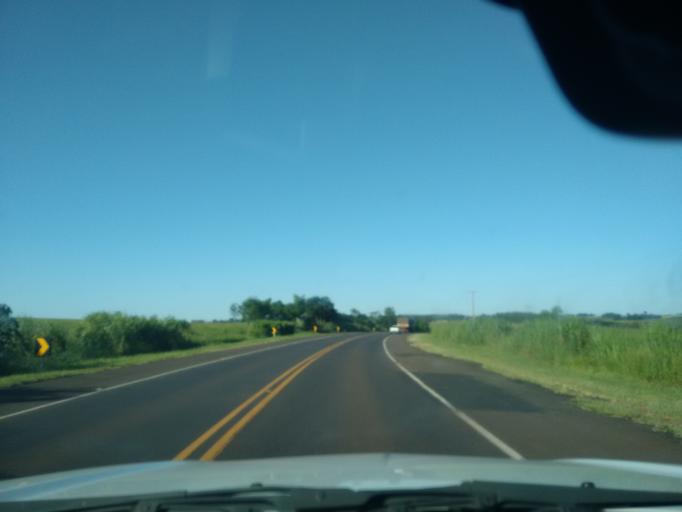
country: PY
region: Canindeyu
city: Salto del Guaira
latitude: -23.9706
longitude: -54.3303
